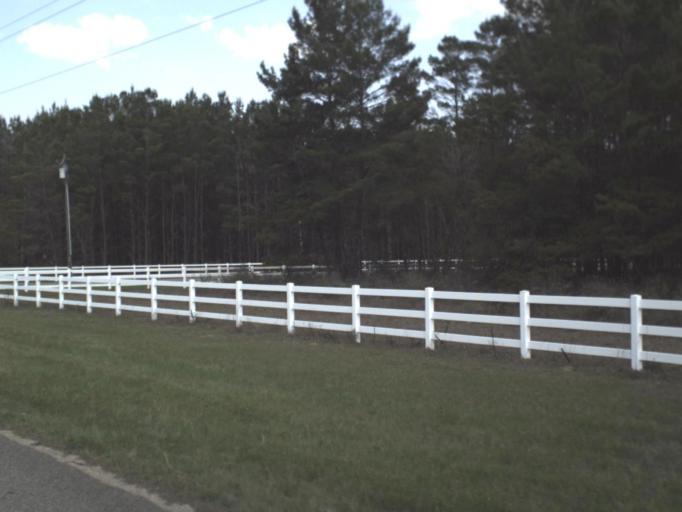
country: US
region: Florida
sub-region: Liberty County
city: Bristol
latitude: 30.4218
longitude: -84.9067
